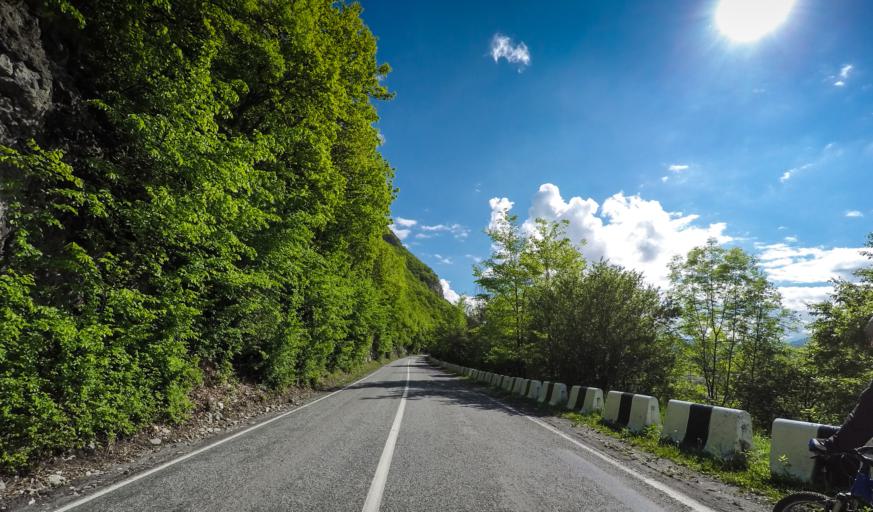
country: RU
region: North Ossetia
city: Vladikavkaz
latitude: 42.9364
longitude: 44.6450
